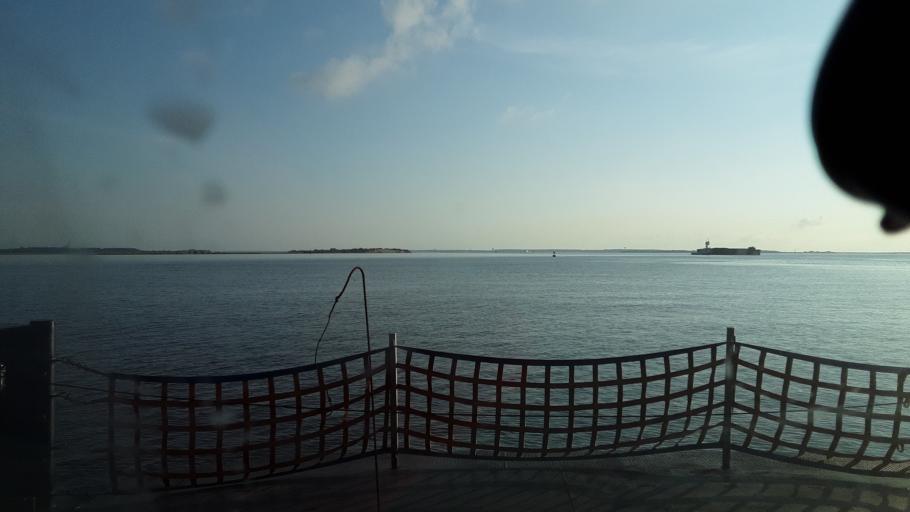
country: US
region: North Carolina
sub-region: Brunswick County
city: Southport
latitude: 33.9424
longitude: -77.9750
